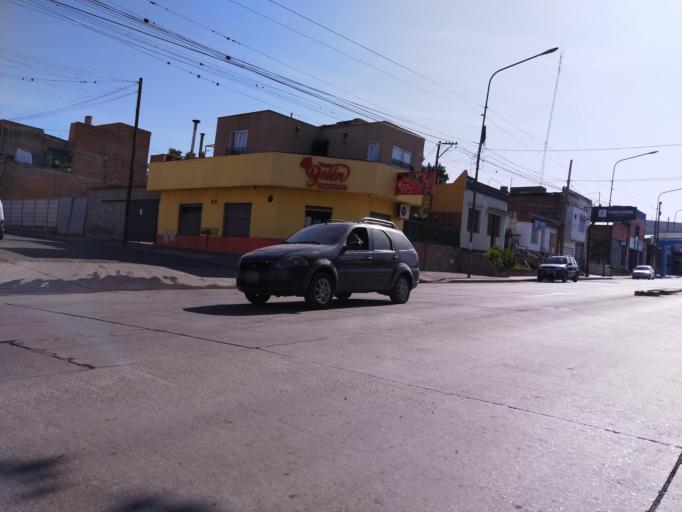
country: AR
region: Jujuy
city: San Salvador de Jujuy
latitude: -24.2015
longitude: -65.2847
